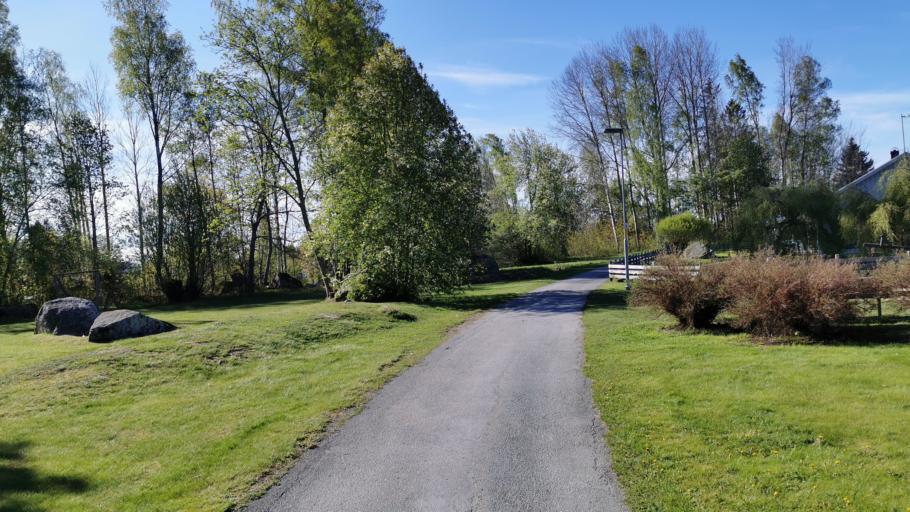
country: SE
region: OErebro
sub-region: Orebro Kommun
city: Hovsta
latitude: 59.3165
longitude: 15.2157
